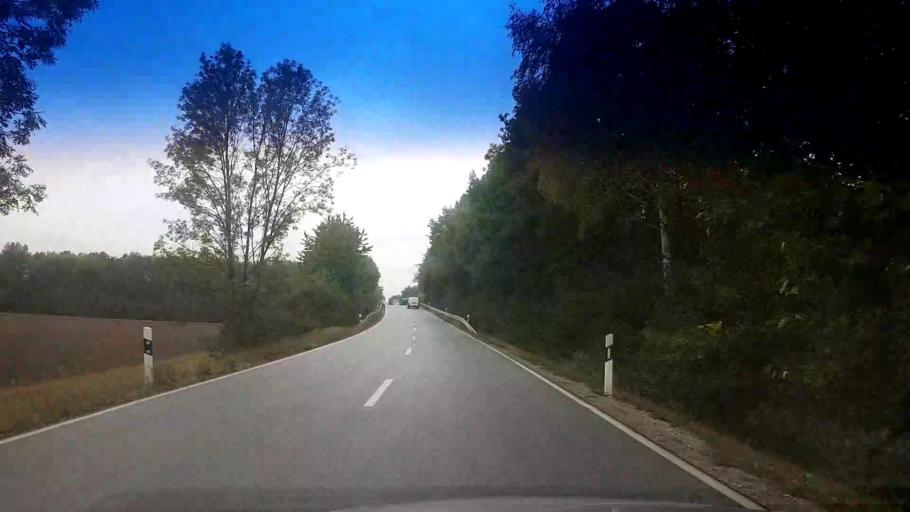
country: DE
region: Bavaria
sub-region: Upper Franconia
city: Eggolsheim
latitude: 49.7748
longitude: 11.0475
